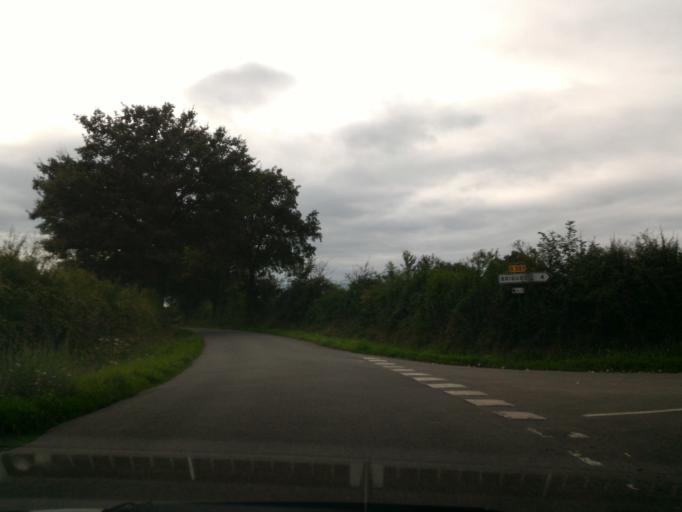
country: FR
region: Poitou-Charentes
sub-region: Departement de la Charente
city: Brigueuil
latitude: 45.9324
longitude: 0.8222
